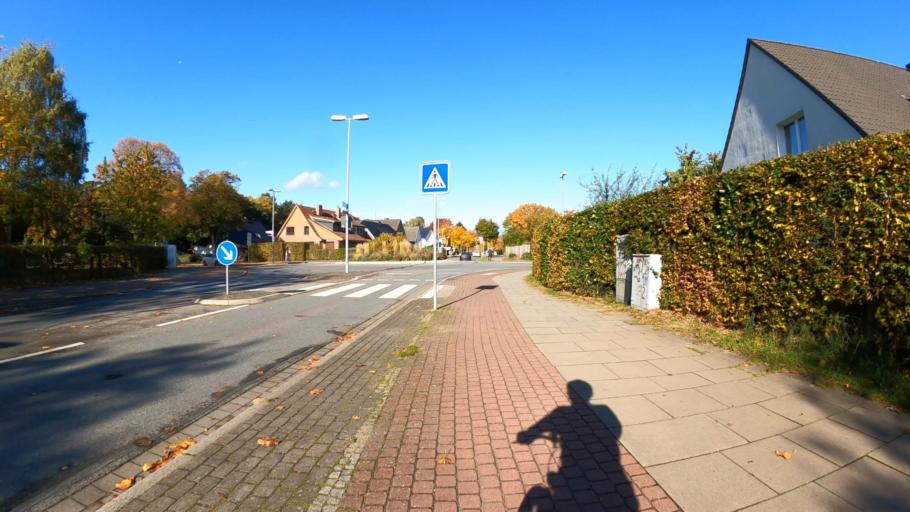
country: DE
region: Schleswig-Holstein
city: Ahrensburg
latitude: 53.6740
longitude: 10.2293
